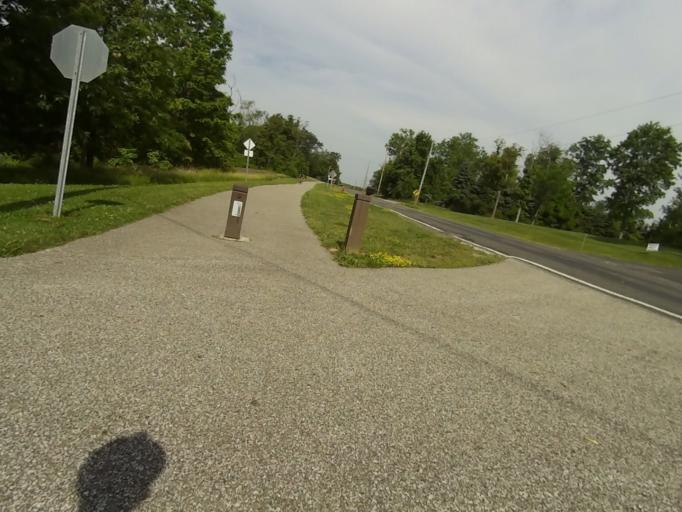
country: US
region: Ohio
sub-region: Summit County
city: Boston Heights
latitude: 41.2746
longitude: -81.5345
